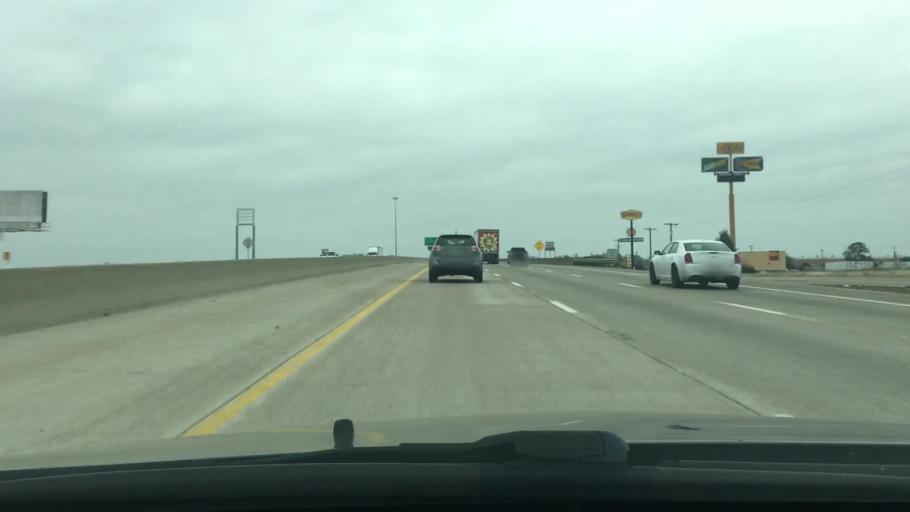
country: US
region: Texas
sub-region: Dallas County
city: Wilmer
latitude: 32.5945
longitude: -96.6809
